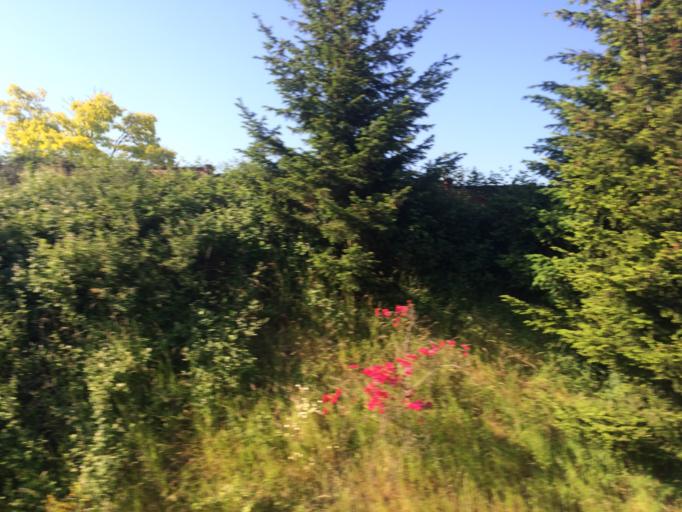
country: CA
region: British Columbia
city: Victoria
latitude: 48.4641
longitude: -123.4254
